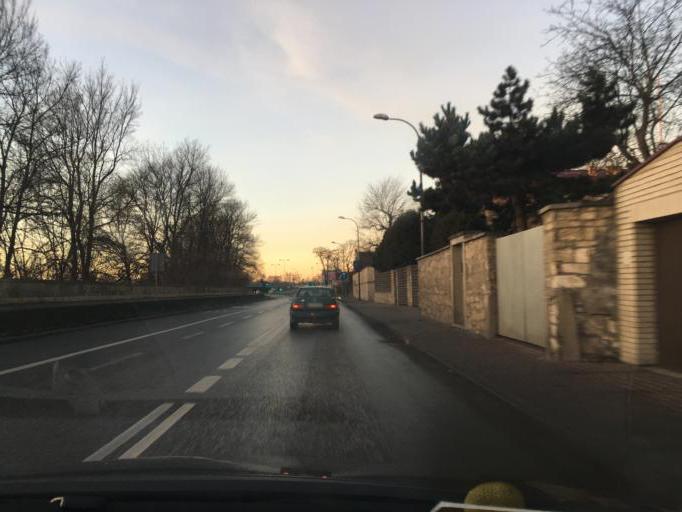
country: PL
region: Lesser Poland Voivodeship
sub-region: Krakow
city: Krakow
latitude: 50.0510
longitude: 19.9078
